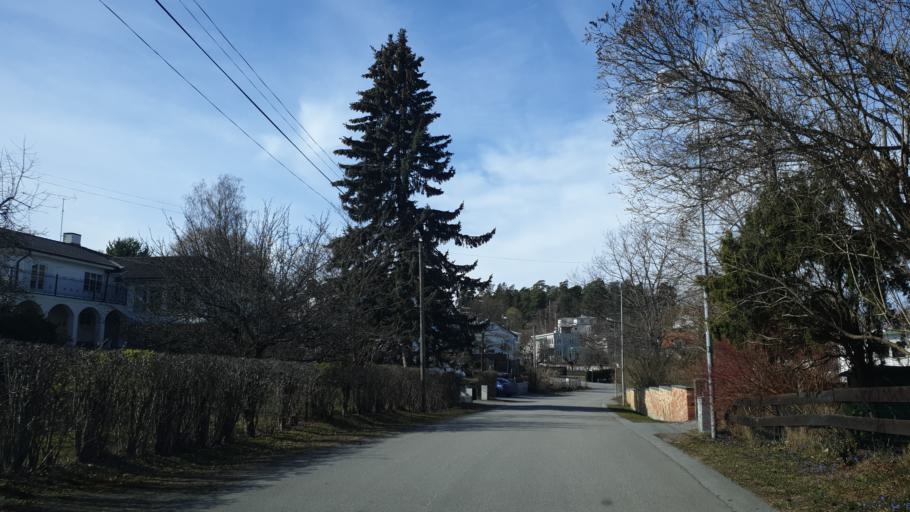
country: SE
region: Stockholm
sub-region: Sollentuna Kommun
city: Sollentuna
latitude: 59.4190
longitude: 17.9817
